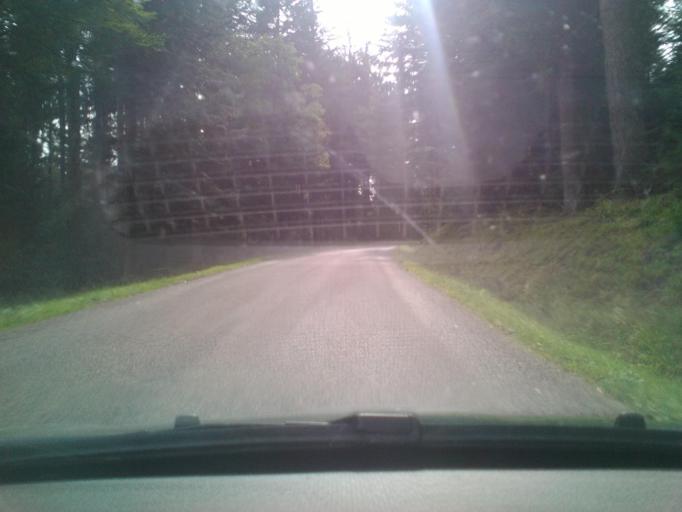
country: FR
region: Lorraine
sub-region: Departement des Vosges
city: Plainfaing
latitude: 48.1448
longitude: 7.0671
